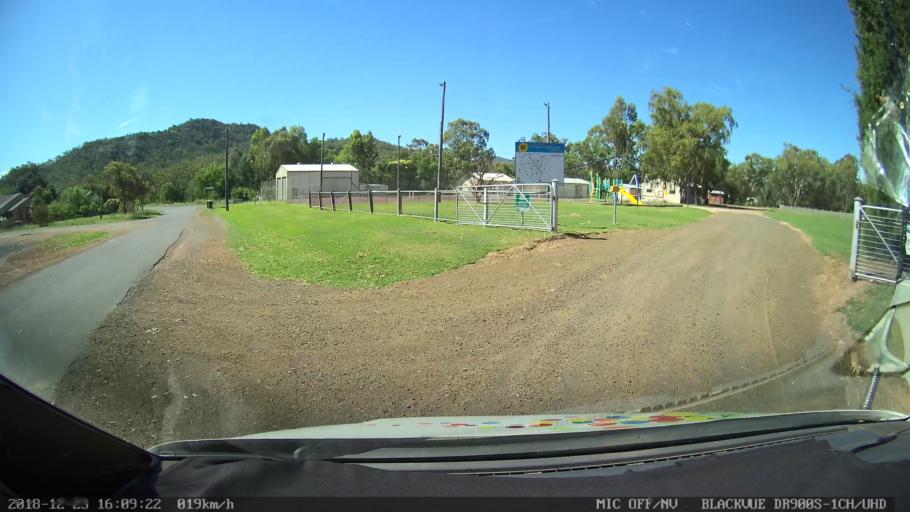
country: AU
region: New South Wales
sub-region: Tamworth Municipality
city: Phillip
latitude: -31.2613
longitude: 150.7395
